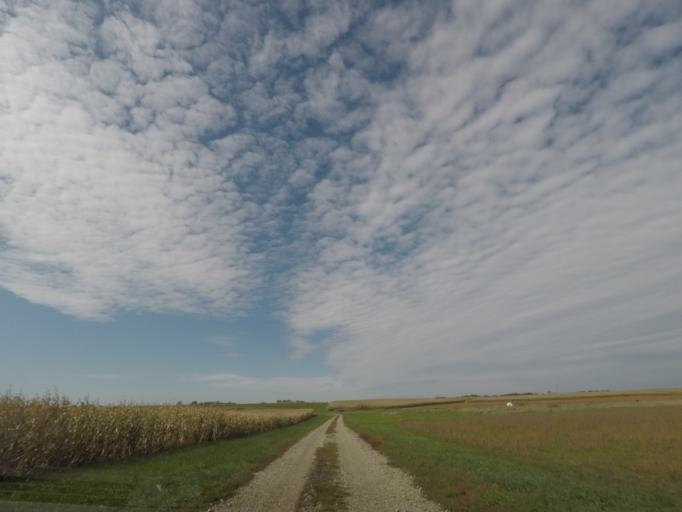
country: US
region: Iowa
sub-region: Boone County
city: Boone
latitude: 42.0161
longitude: -93.7796
